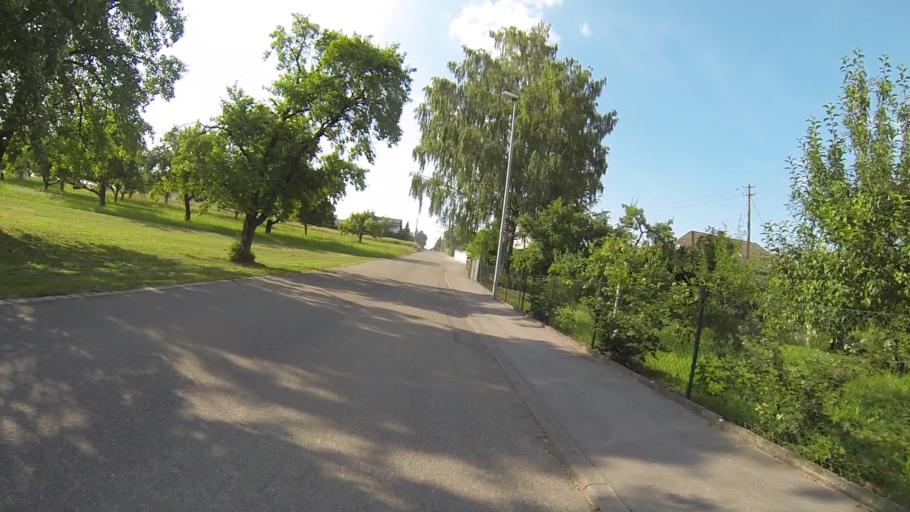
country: DE
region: Baden-Wuerttemberg
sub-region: Regierungsbezirk Stuttgart
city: Niederstotzingen
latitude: 48.5348
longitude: 10.2330
